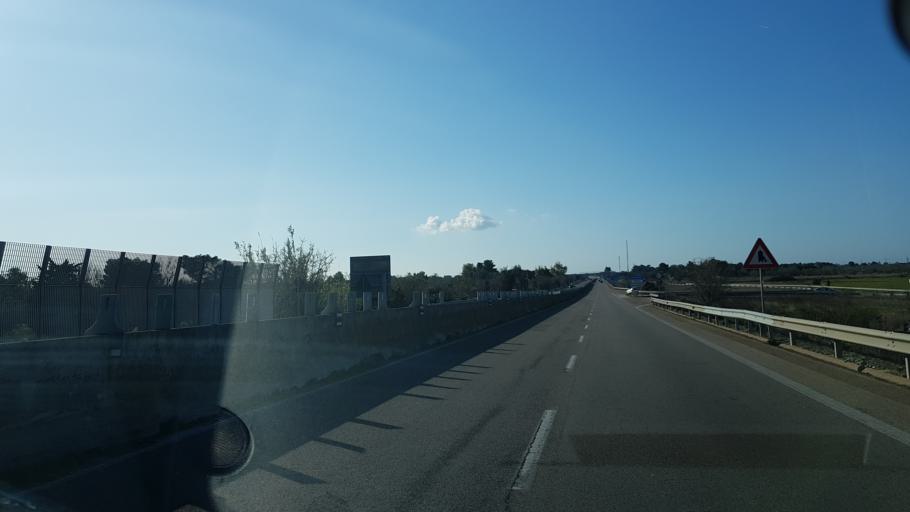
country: IT
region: Apulia
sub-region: Provincia di Lecce
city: Sannicola
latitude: 40.1091
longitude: 18.0379
